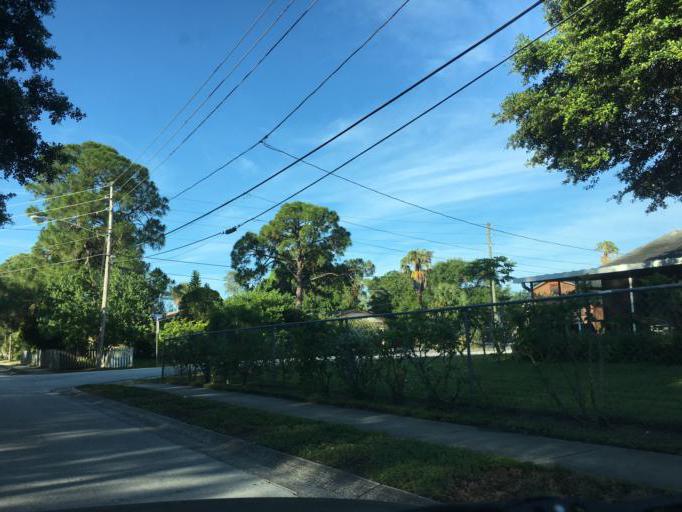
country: US
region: Florida
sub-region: Pinellas County
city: Pinellas Park
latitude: 27.8372
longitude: -82.7040
